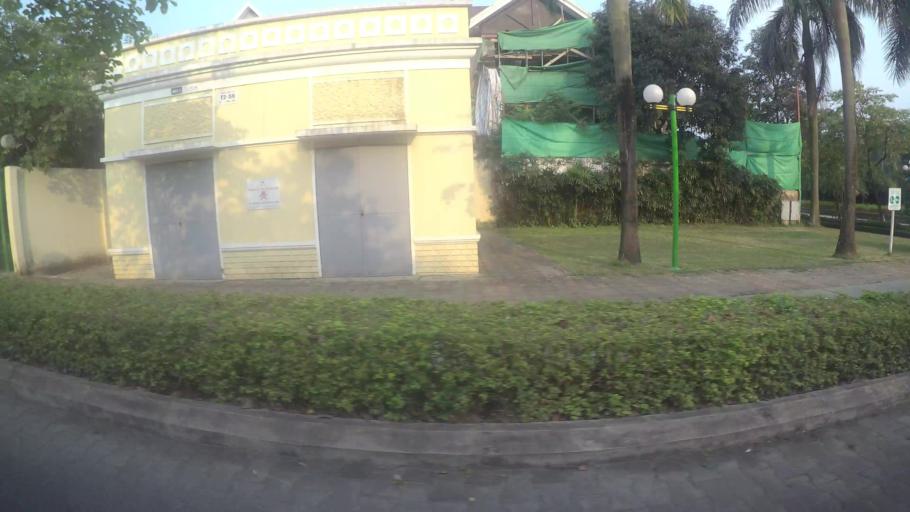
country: VN
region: Ha Noi
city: Tay Ho
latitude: 21.0776
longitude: 105.7948
